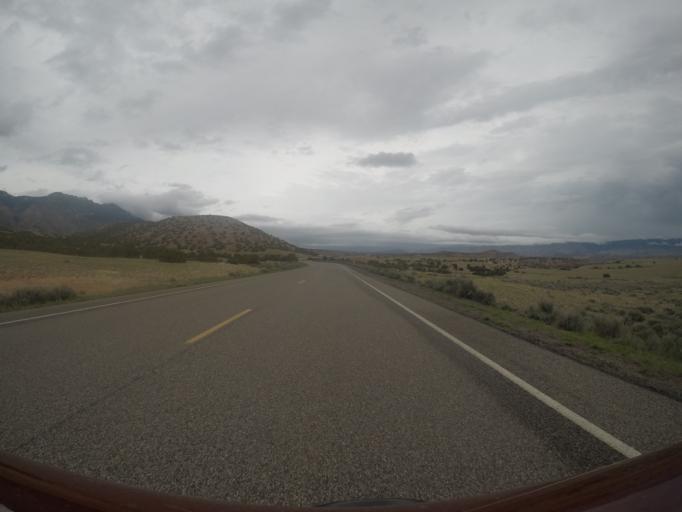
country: US
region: Wyoming
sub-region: Big Horn County
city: Lovell
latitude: 45.0638
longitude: -108.2571
